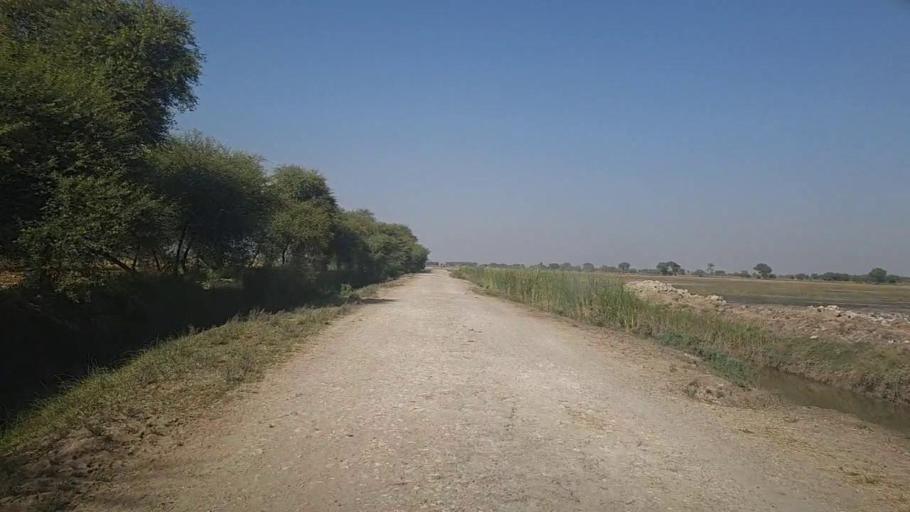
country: PK
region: Sindh
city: Thul
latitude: 28.3042
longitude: 68.7710
